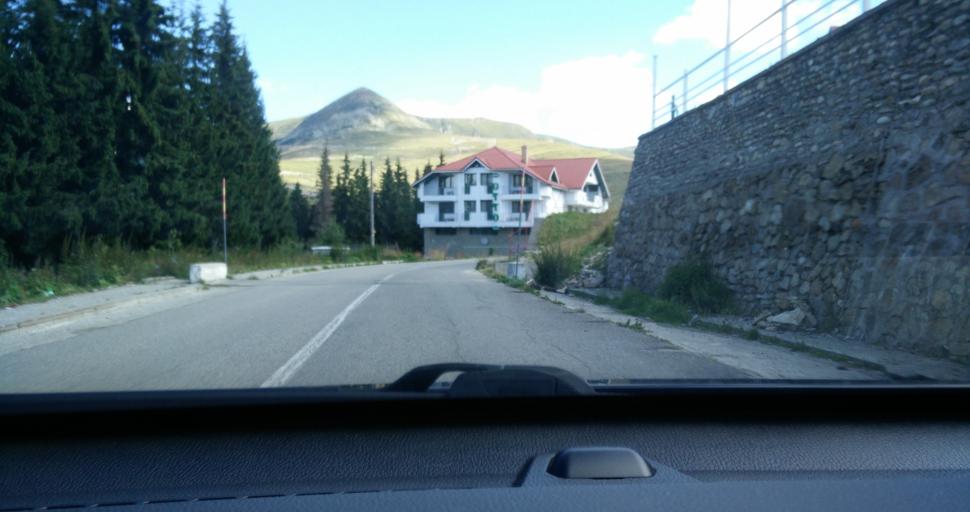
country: RO
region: Gorj
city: Novaci-Straini
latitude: 45.3027
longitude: 23.6822
